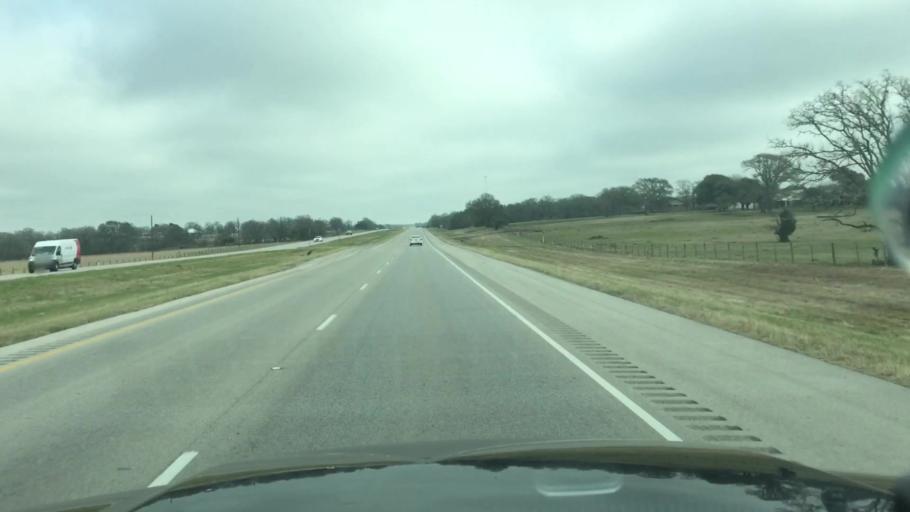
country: US
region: Texas
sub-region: Lee County
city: Giddings
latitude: 30.1454
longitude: -96.7208
